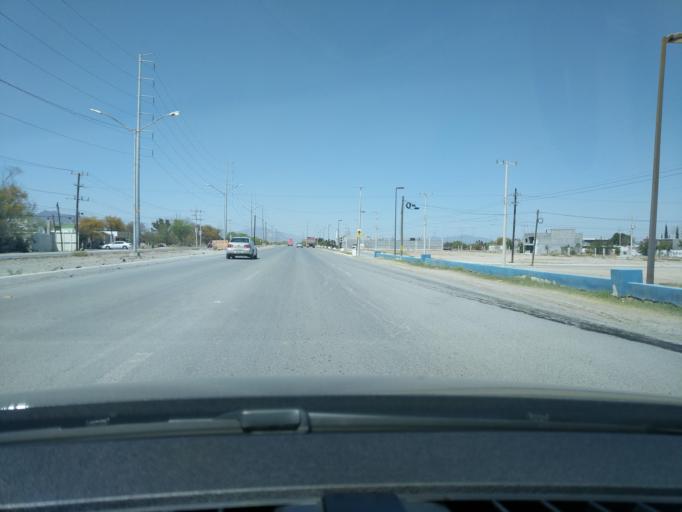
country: MX
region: Nuevo Leon
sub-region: Salinas Victoria
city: Emiliano Zapata
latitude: 25.9151
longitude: -100.2686
